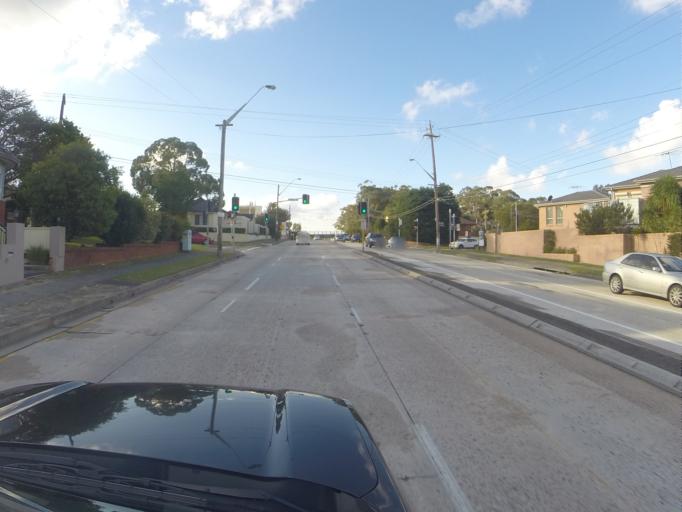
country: AU
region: New South Wales
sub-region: Kogarah
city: Kogarah
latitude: -33.9843
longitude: 151.1137
